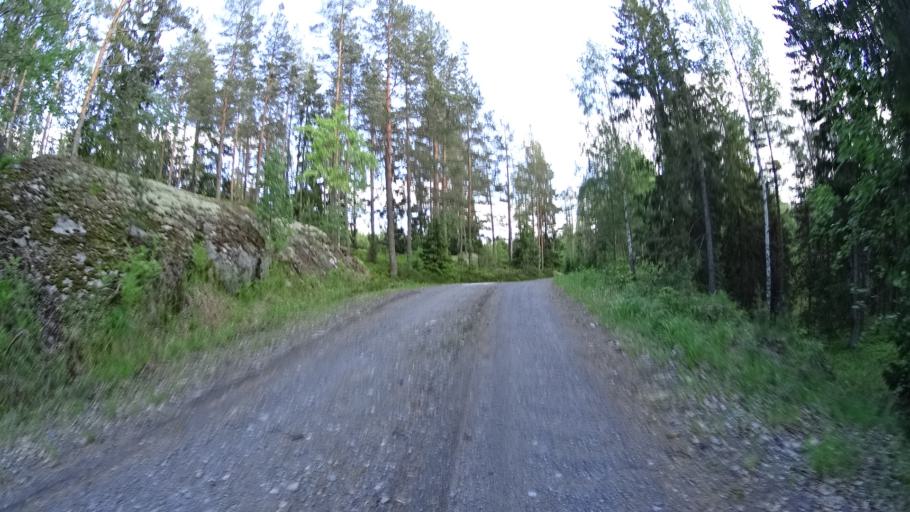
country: FI
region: Varsinais-Suomi
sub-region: Salo
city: Kisko
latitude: 60.1615
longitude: 23.4904
